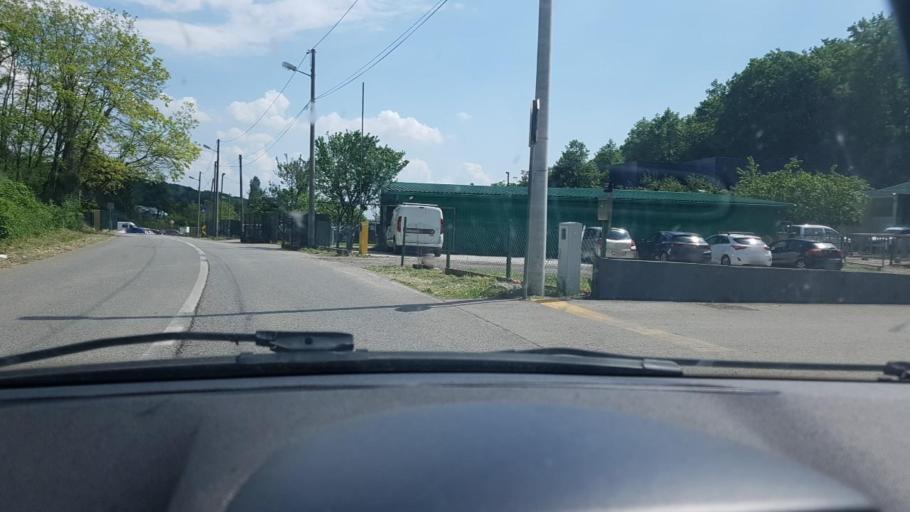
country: HR
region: Grad Zagreb
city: Dubrava
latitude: 45.8582
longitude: 16.0245
